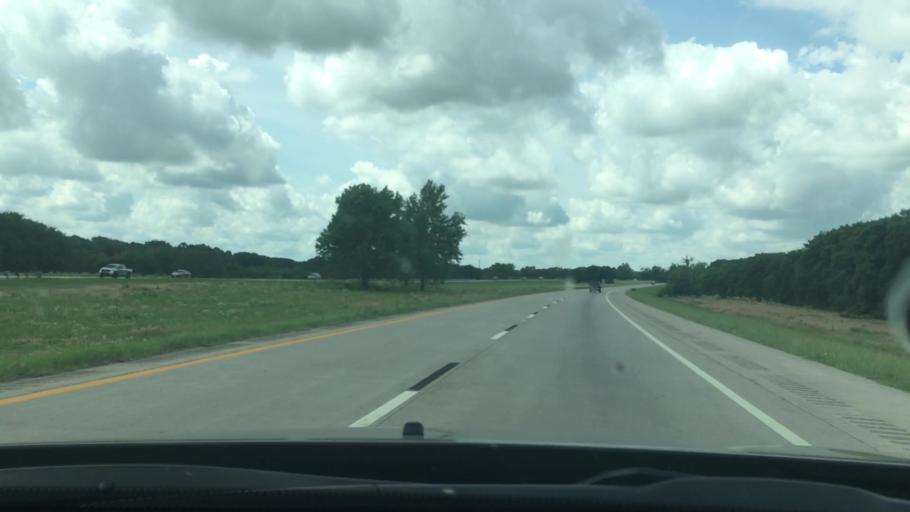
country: US
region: Oklahoma
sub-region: Love County
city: Marietta
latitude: 33.8245
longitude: -97.1305
